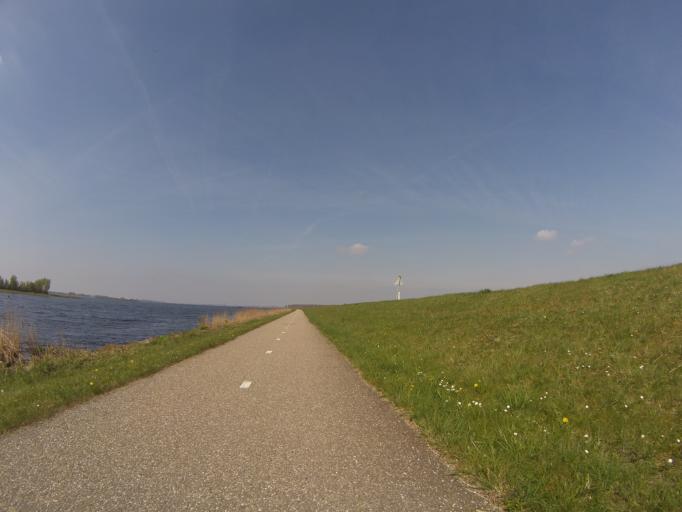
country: NL
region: North Holland
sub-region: Gemeente Huizen
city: Huizen
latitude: 52.3051
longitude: 5.3142
